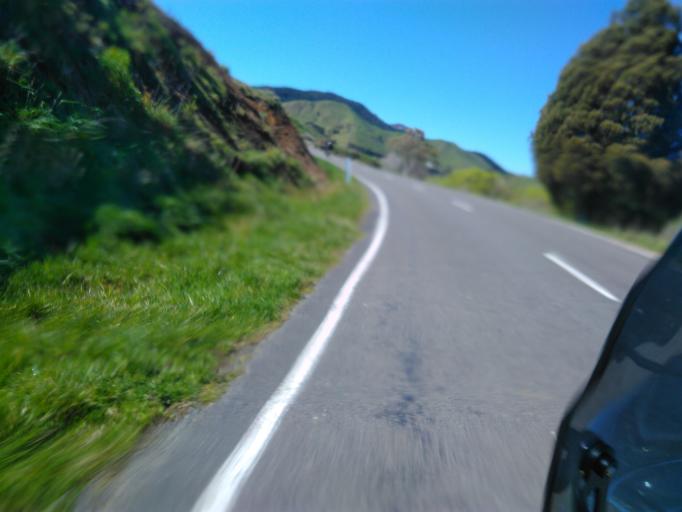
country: NZ
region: Bay of Plenty
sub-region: Opotiki District
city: Opotiki
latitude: -38.3082
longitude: 177.5204
